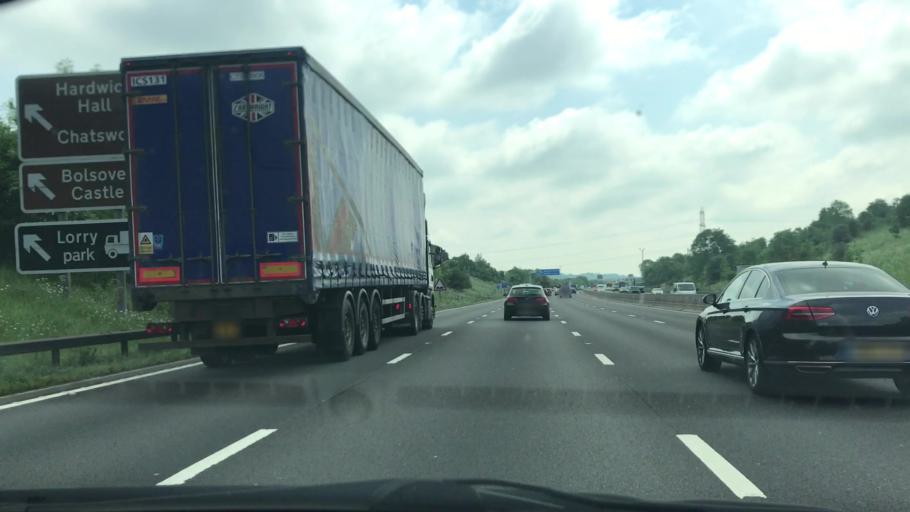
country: GB
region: England
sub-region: Derbyshire
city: Bolsover
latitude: 53.2150
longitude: -1.3244
